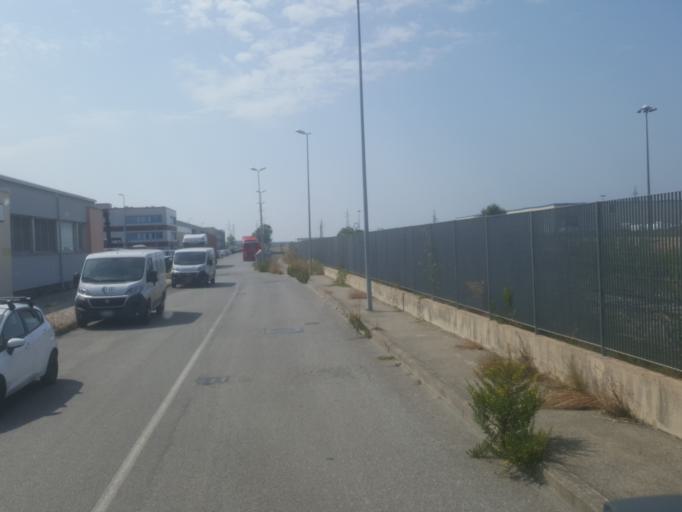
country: IT
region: Tuscany
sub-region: Provincia di Livorno
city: Guasticce
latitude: 43.5950
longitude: 10.3974
